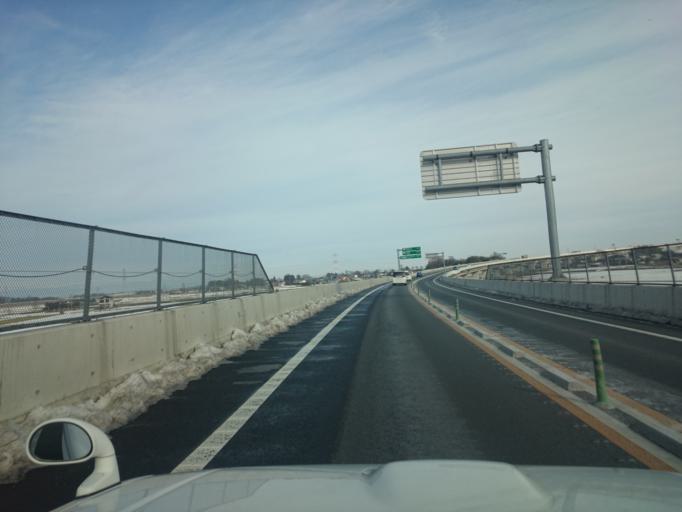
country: JP
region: Ibaraki
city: Sakai
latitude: 36.1060
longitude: 139.7566
